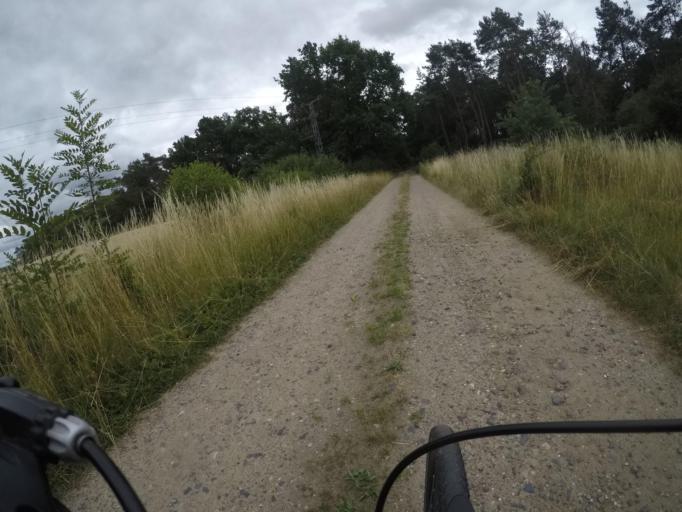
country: DE
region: Lower Saxony
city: Neu Darchau
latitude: 53.2658
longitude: 10.9169
